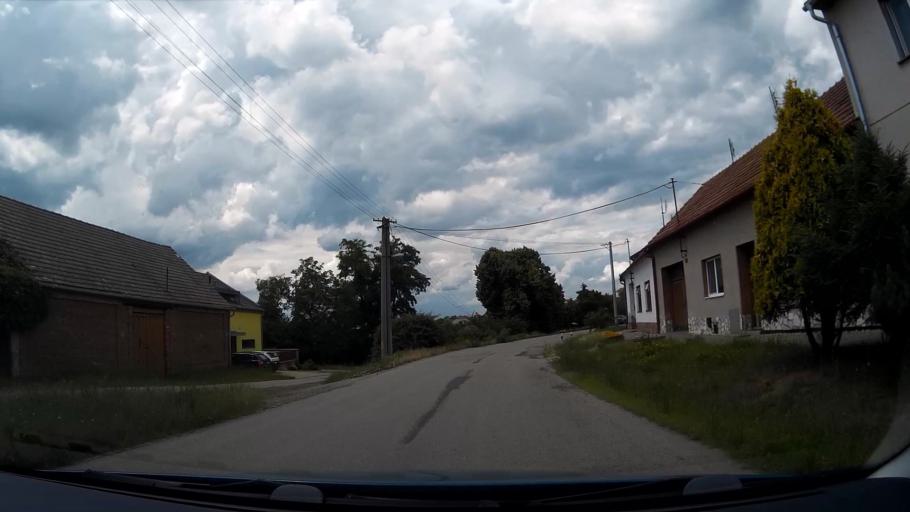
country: CZ
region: South Moravian
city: Orechov
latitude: 49.1115
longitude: 16.5257
